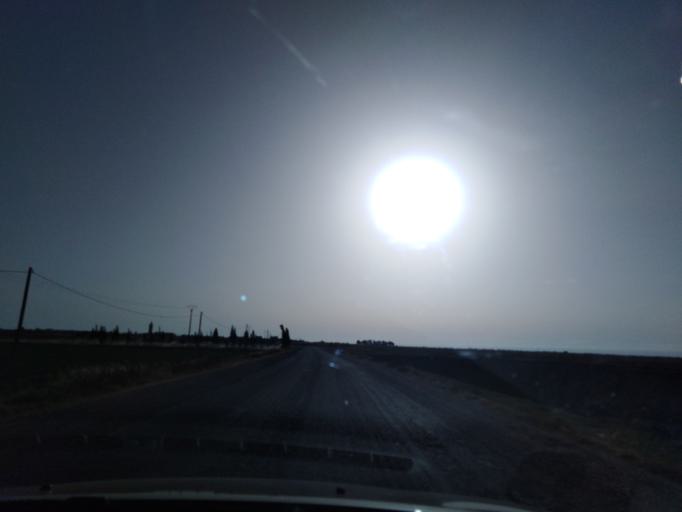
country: MA
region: Doukkala-Abda
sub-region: Safi
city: Safi
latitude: 32.4781
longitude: -8.8851
